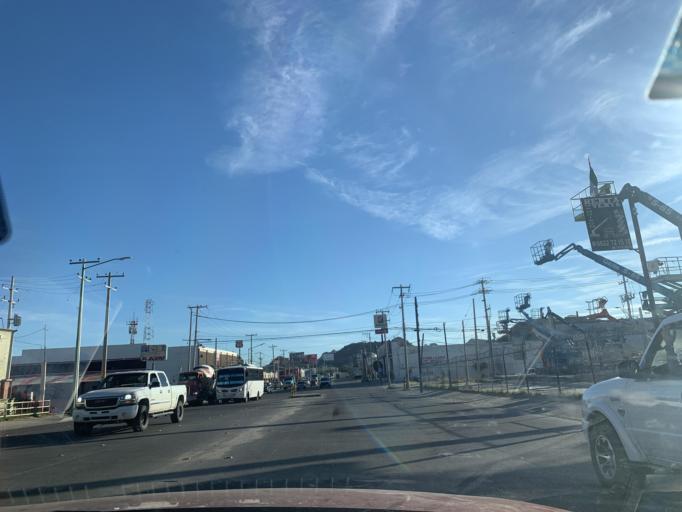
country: MX
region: Sonora
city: Hermosillo
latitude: 29.0968
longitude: -110.9311
